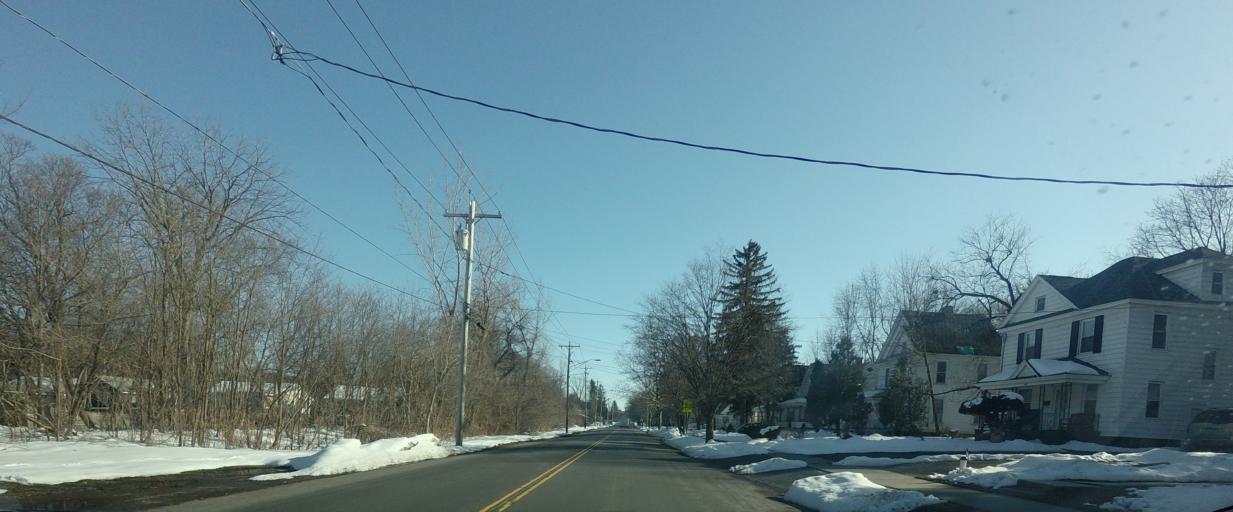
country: US
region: New York
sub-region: Onondaga County
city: Nedrow
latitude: 43.0085
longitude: -76.1476
